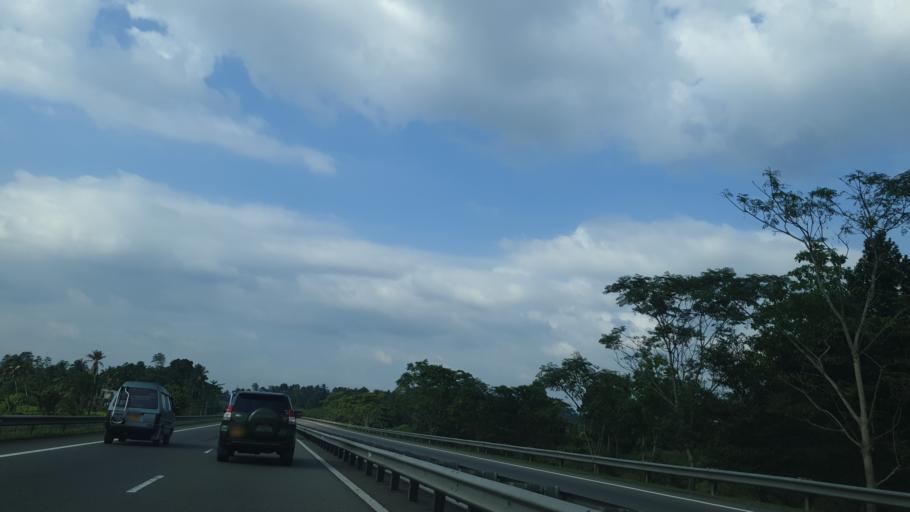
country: LK
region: Western
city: Horana South
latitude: 6.7420
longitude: 79.9980
